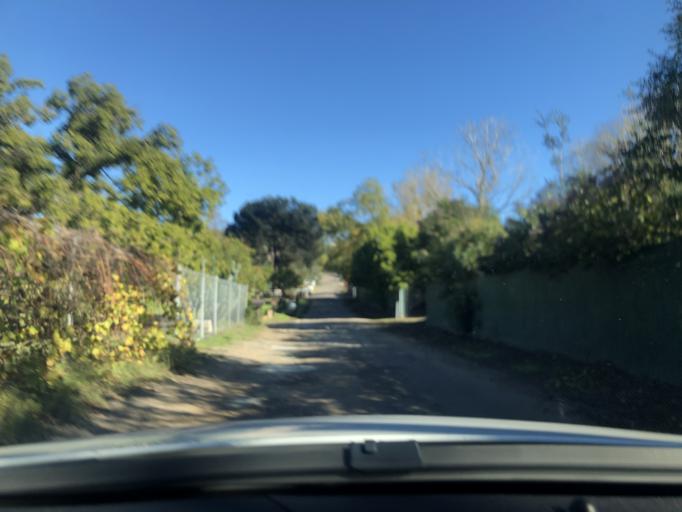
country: US
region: California
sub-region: San Diego County
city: El Cajon
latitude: 32.7769
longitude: -116.9412
